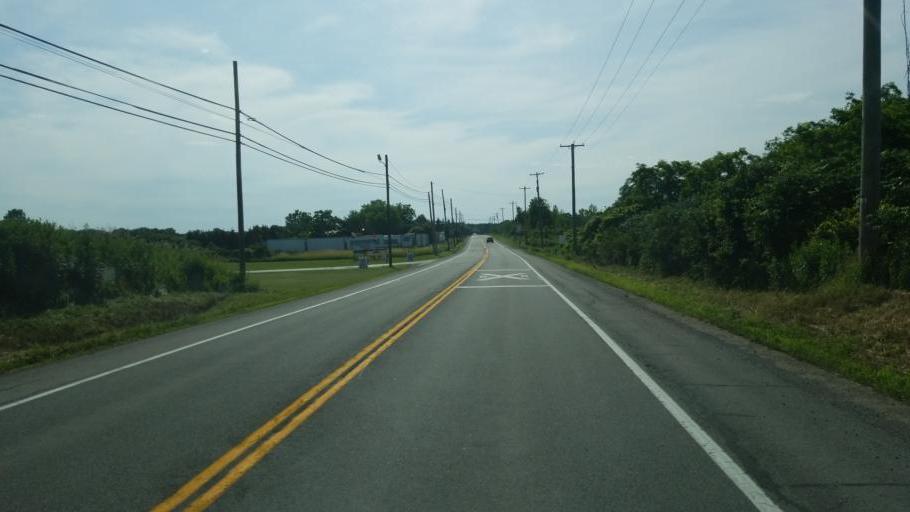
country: US
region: New York
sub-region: Livingston County
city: Caledonia
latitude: 42.9778
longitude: -77.8809
